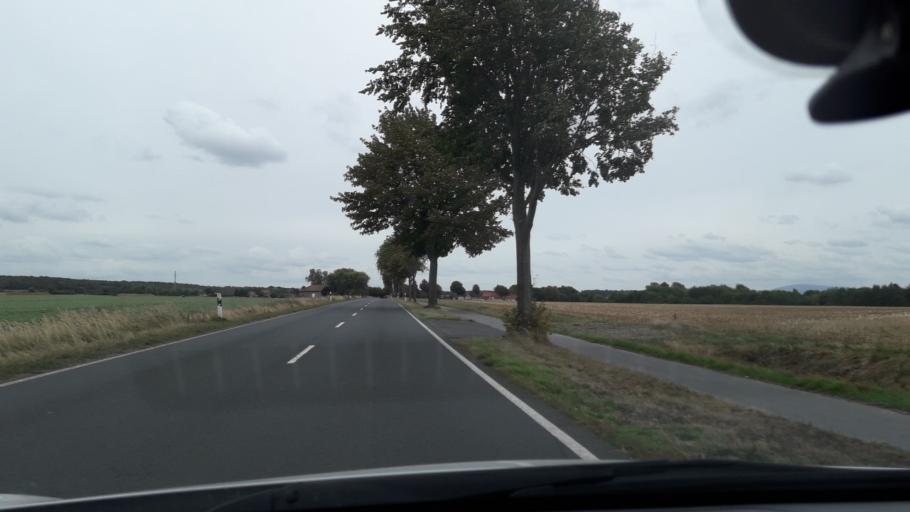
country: DE
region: Lower Saxony
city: Flothe
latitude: 52.0828
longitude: 10.4786
